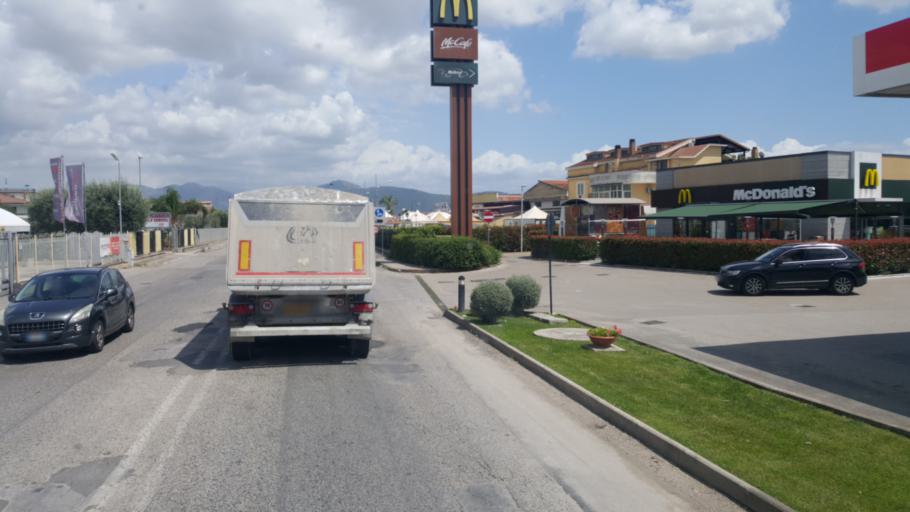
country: IT
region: Campania
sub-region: Provincia di Caserta
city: Maddaloni
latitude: 41.0253
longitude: 14.3721
